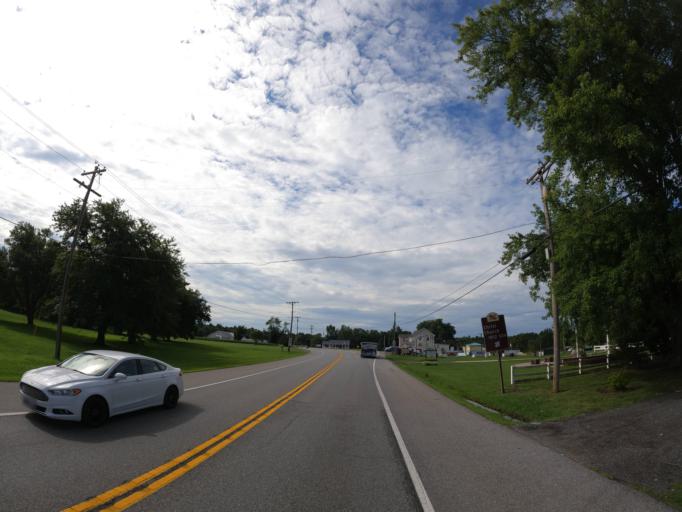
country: US
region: Maryland
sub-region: Saint Mary's County
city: Mechanicsville
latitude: 38.3857
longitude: -76.7217
